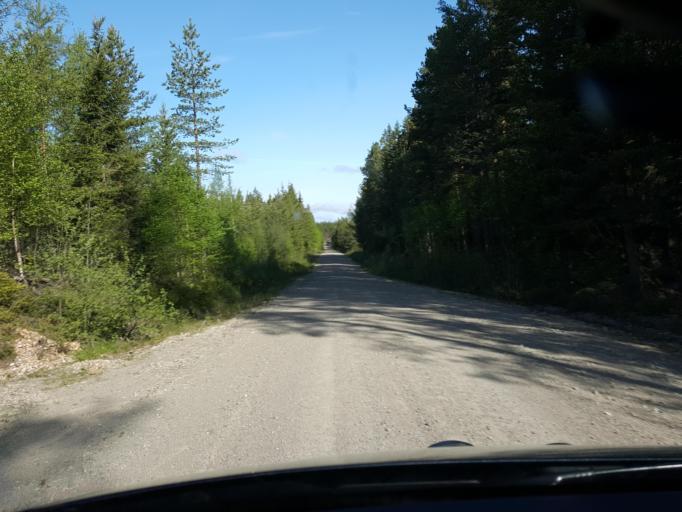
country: SE
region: Vaesternorrland
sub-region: Ange Kommun
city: Ange
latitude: 62.1871
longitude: 15.6011
